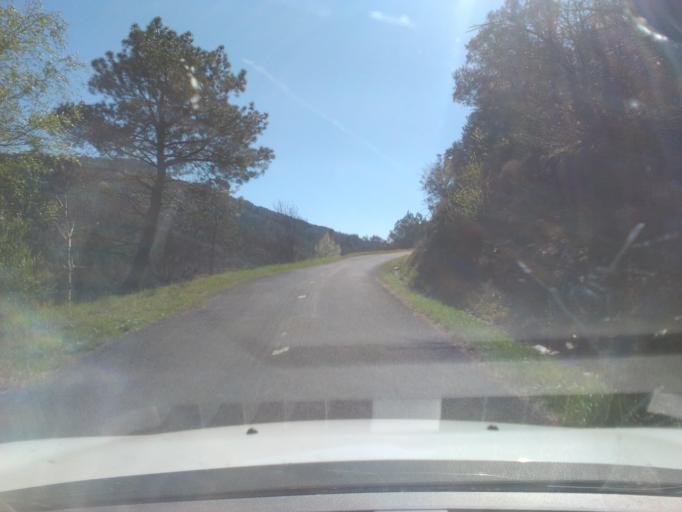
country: FR
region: Languedoc-Roussillon
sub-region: Departement du Gard
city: Valleraugue
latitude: 44.1741
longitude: 3.7520
